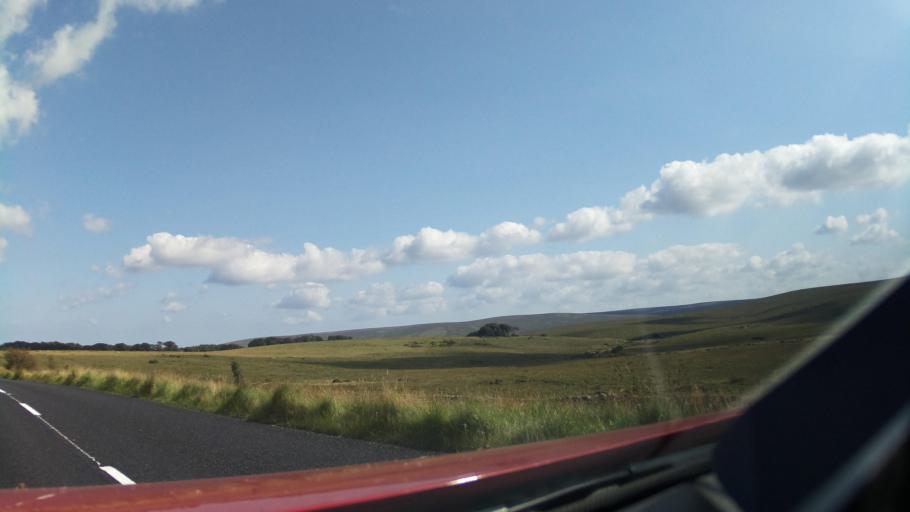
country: GB
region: England
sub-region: Devon
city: Yelverton
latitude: 50.5572
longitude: -3.9574
